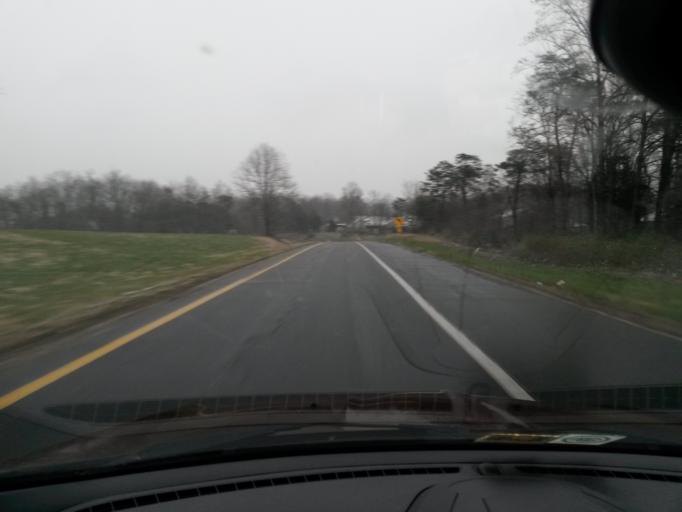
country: US
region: Virginia
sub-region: Campbell County
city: Timberlake
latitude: 37.3091
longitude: -79.2651
